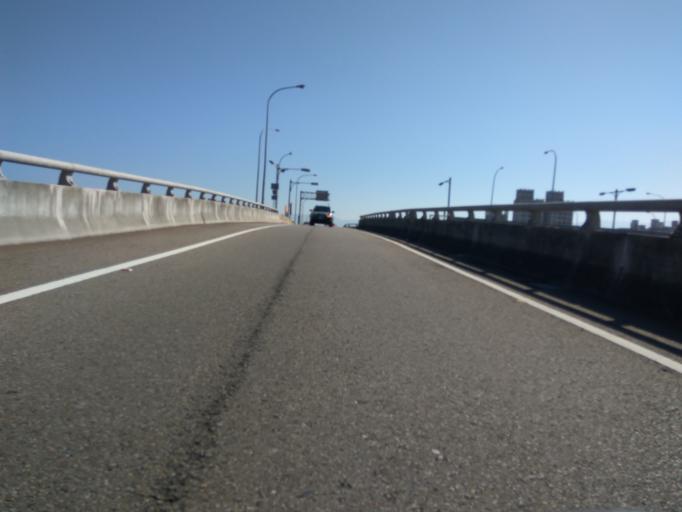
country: TW
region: Taiwan
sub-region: Hsinchu
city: Hsinchu
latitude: 24.8266
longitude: 120.9711
